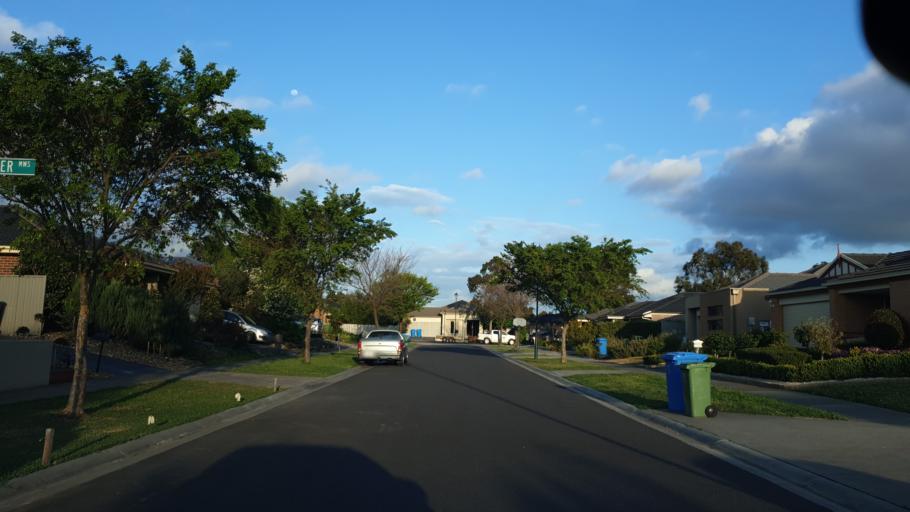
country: AU
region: Victoria
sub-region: Casey
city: Cranbourne East
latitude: -38.1078
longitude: 145.3065
